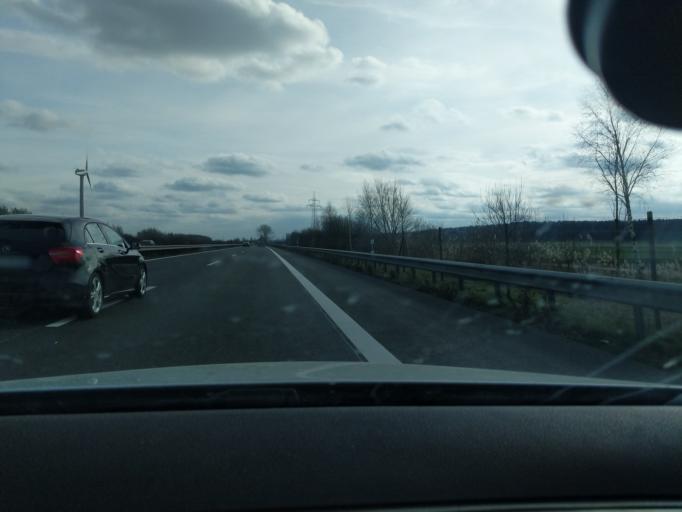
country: DE
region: Lower Saxony
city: Agathenburg
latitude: 53.5614
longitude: 9.5575
